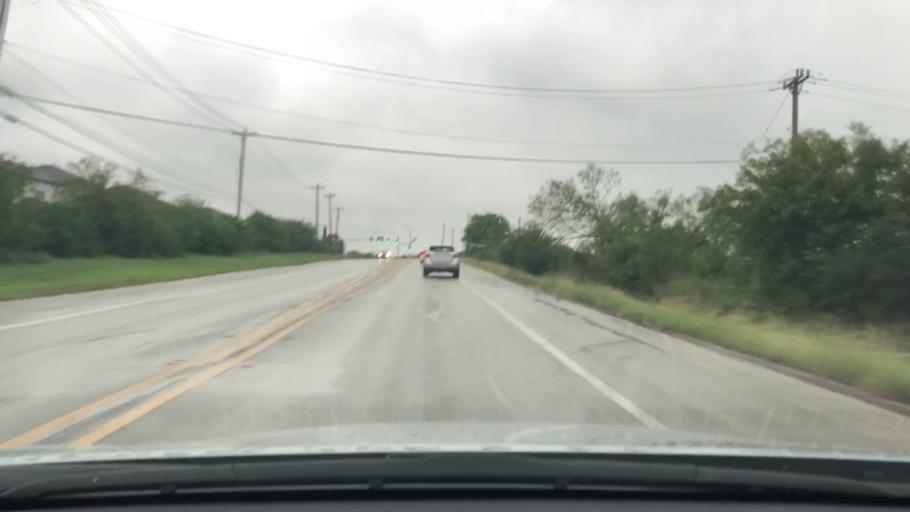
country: US
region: Texas
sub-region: Bexar County
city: Converse
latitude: 29.4879
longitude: -98.3107
